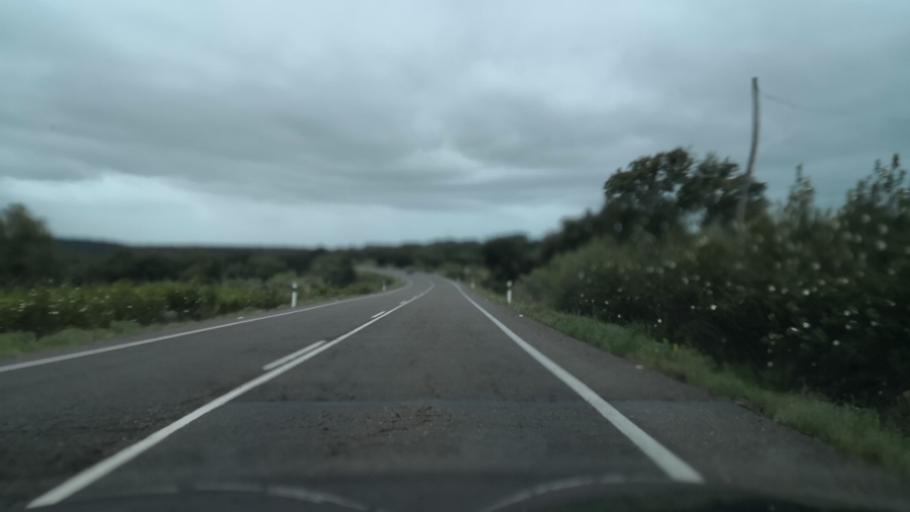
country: ES
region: Extremadura
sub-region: Provincia de Badajoz
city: Puebla de Obando
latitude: 39.1498
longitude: -6.6503
